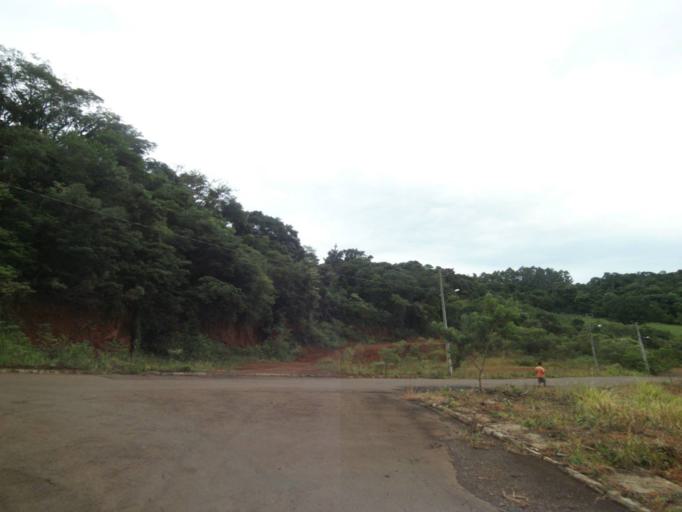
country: BR
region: Parana
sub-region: Guaraniacu
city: Guaraniacu
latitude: -25.0992
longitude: -52.8866
